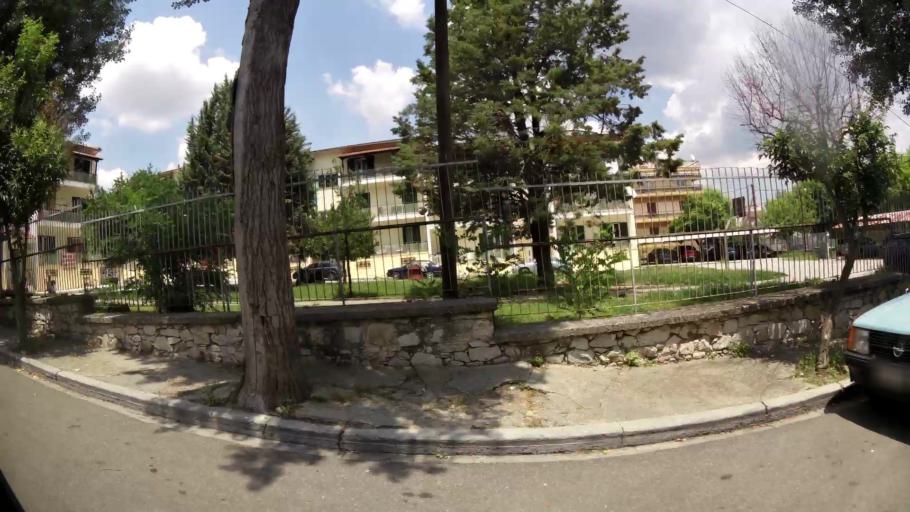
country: GR
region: West Macedonia
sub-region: Nomos Kozanis
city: Kozani
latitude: 40.2947
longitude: 21.7826
